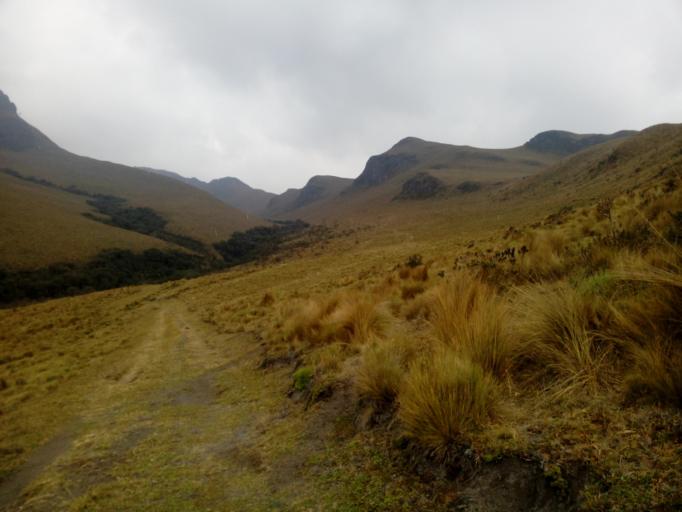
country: EC
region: Pichincha
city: Machachi
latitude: -0.5585
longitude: -78.5276
